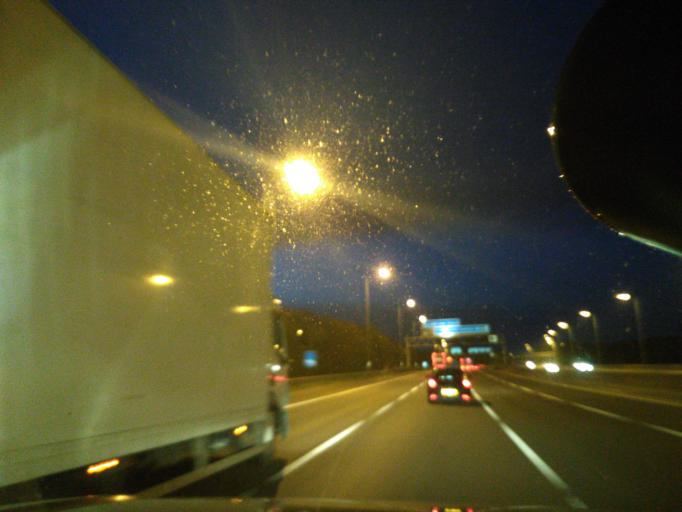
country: GB
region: England
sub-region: Nottinghamshire
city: Kirkby in Ashfield
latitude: 53.0686
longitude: -1.2754
